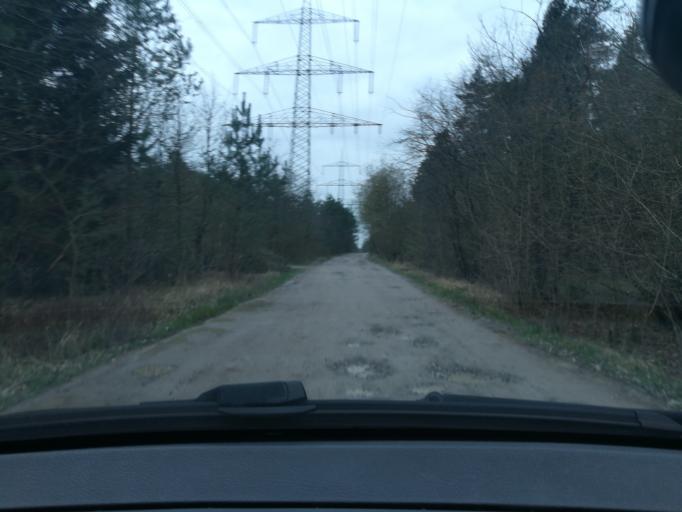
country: DE
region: North Rhine-Westphalia
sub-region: Regierungsbezirk Detmold
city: Oerlinghausen
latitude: 51.9481
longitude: 8.6182
